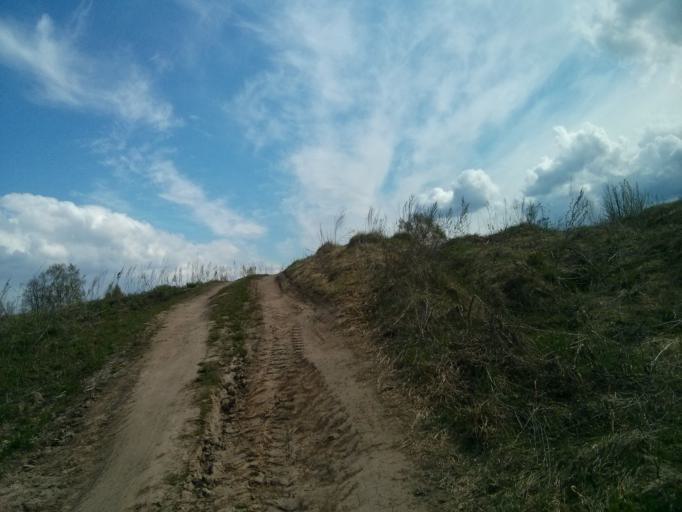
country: RU
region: Nizjnij Novgorod
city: Shimorskoye
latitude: 55.3042
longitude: 41.8453
